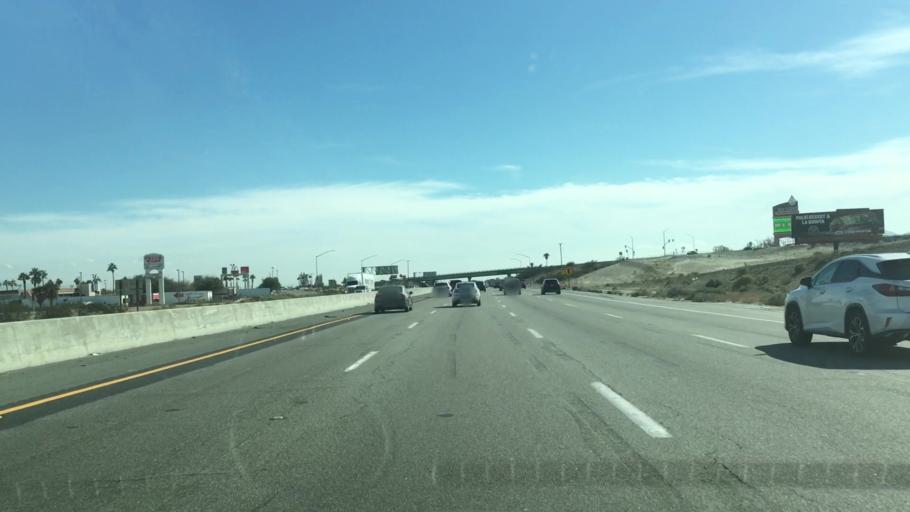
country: US
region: California
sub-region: Riverside County
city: Thousand Palms
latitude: 33.8193
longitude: -116.4081
